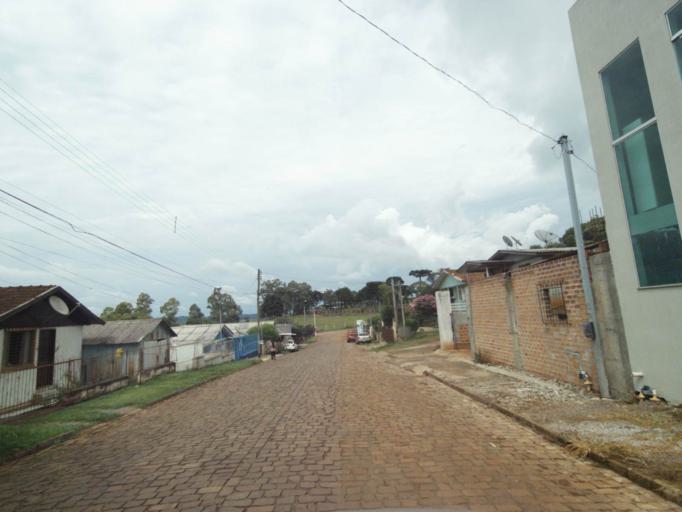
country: BR
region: Rio Grande do Sul
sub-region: Lagoa Vermelha
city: Lagoa Vermelha
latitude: -28.2256
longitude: -51.5148
